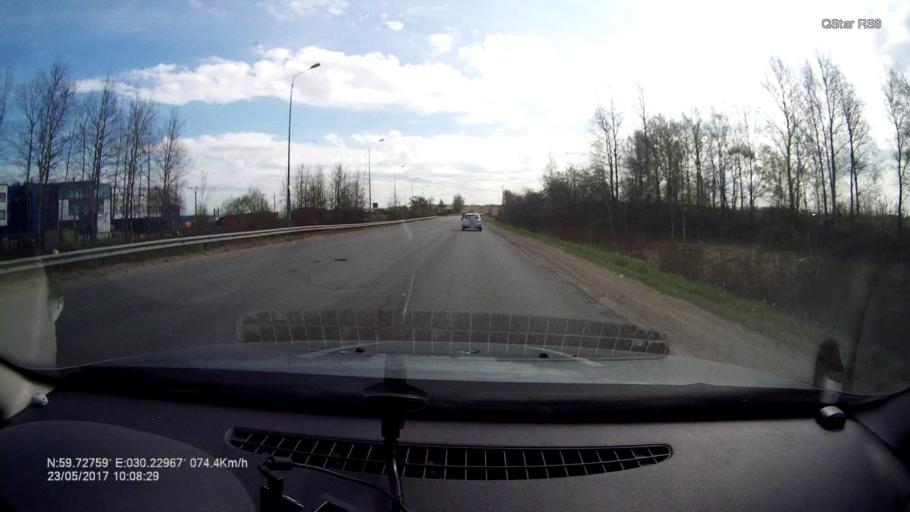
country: RU
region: St.-Petersburg
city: Aleksandrovskaya
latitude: 59.7276
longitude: 30.2301
